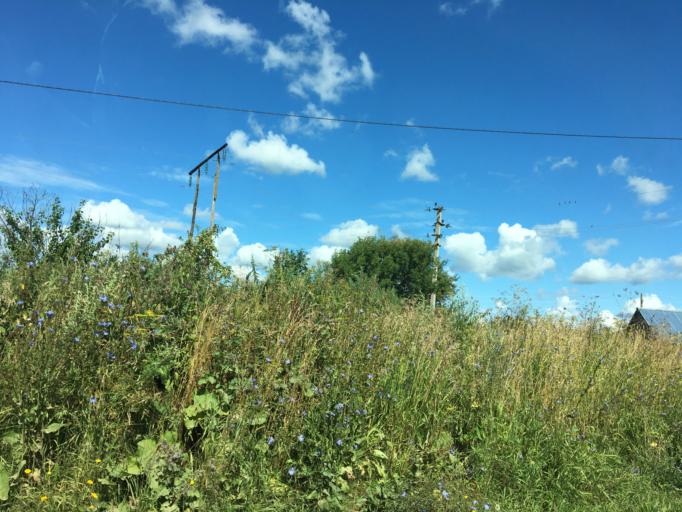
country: RU
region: Nizjnij Novgorod
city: Lyskovo
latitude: 55.9841
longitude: 45.0286
